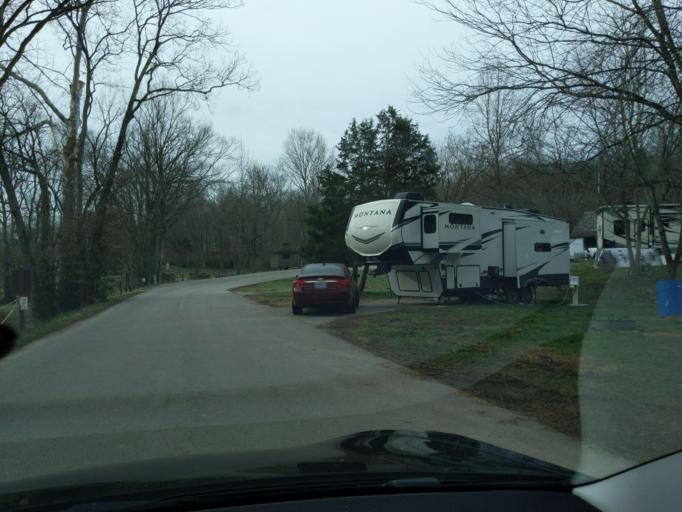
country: US
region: Kentucky
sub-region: Clark County
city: Winchester
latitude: 37.8989
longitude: -84.2680
